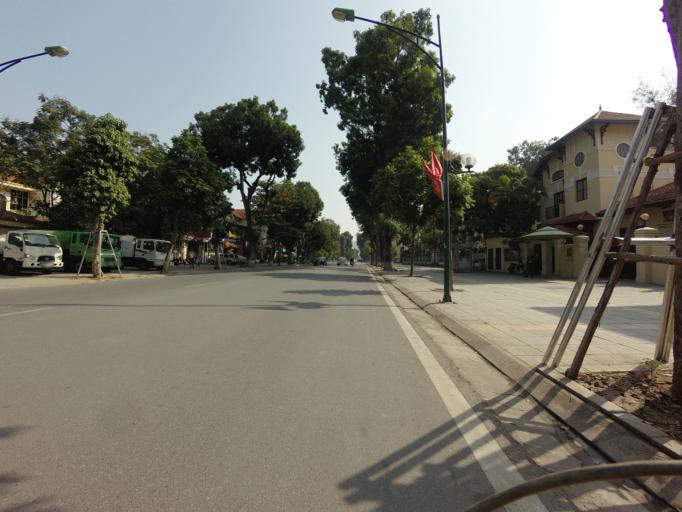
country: VN
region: Ha Noi
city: Hanoi
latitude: 21.0342
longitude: 105.8376
